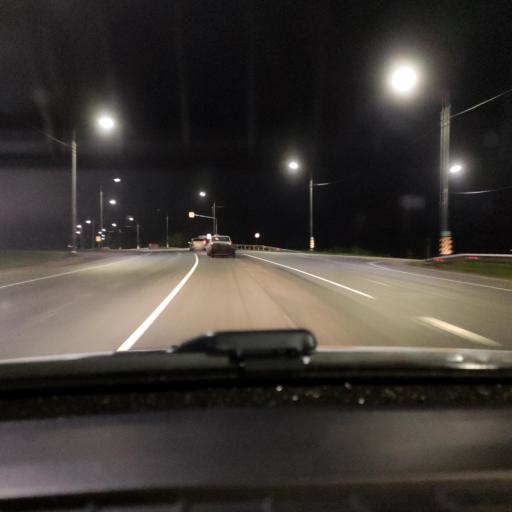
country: RU
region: Voronezj
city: Kashirskoye
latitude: 51.5007
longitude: 39.5678
